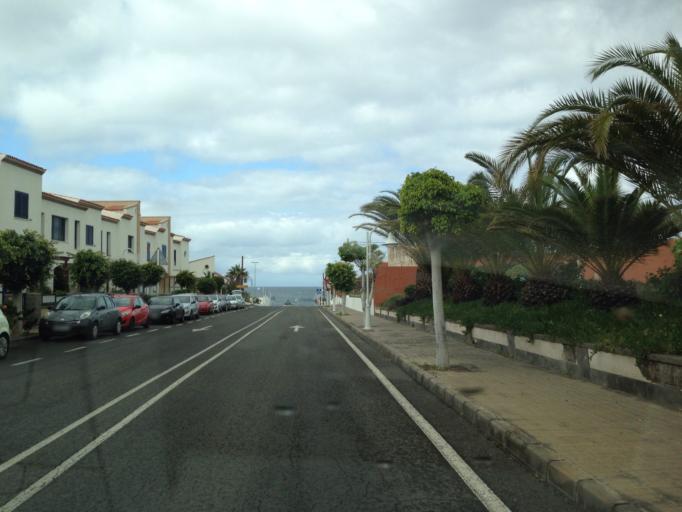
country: ES
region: Canary Islands
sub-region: Provincia de Las Palmas
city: Agaete
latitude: 28.1028
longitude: -15.7105
